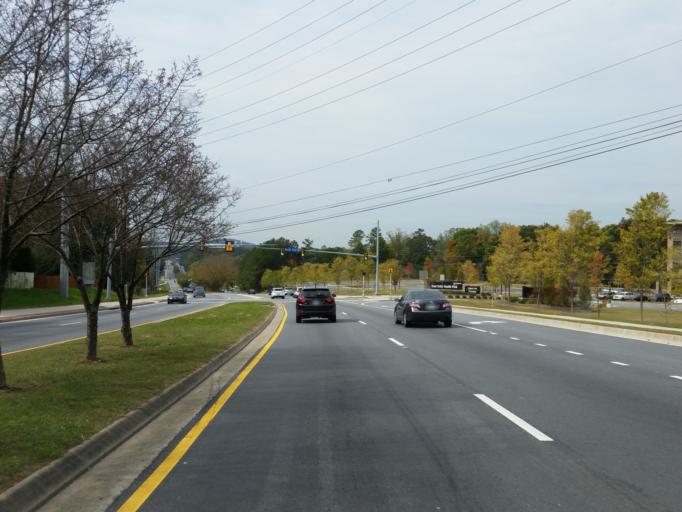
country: US
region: Georgia
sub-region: Fulton County
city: Sandy Springs
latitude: 33.9789
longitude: -84.4436
